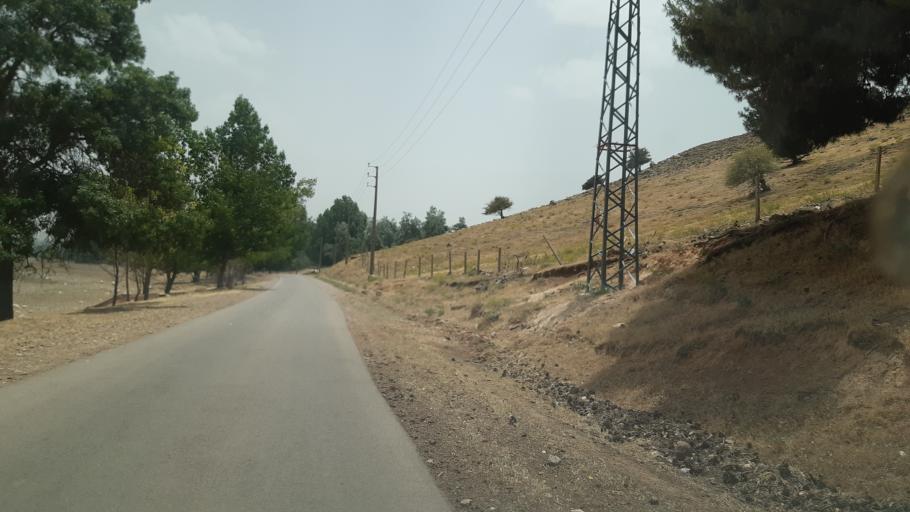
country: MA
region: Meknes-Tafilalet
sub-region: Ifrane
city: Ifrane
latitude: 33.6518
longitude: -5.0407
